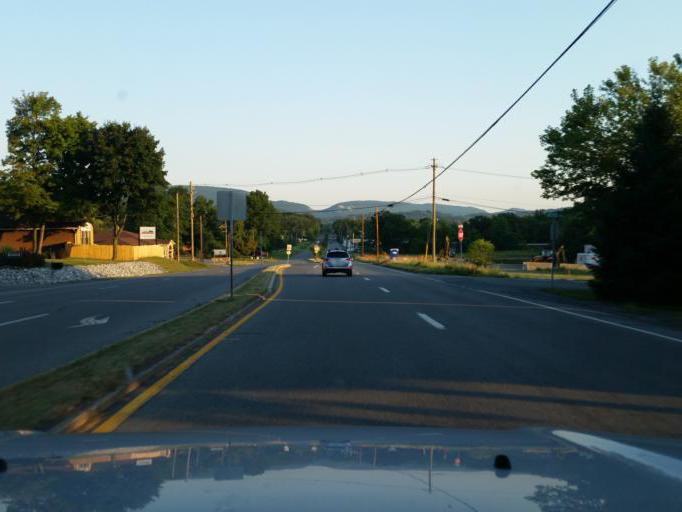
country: US
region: Pennsylvania
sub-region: Blair County
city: Lakemont
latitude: 40.4558
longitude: -78.3947
